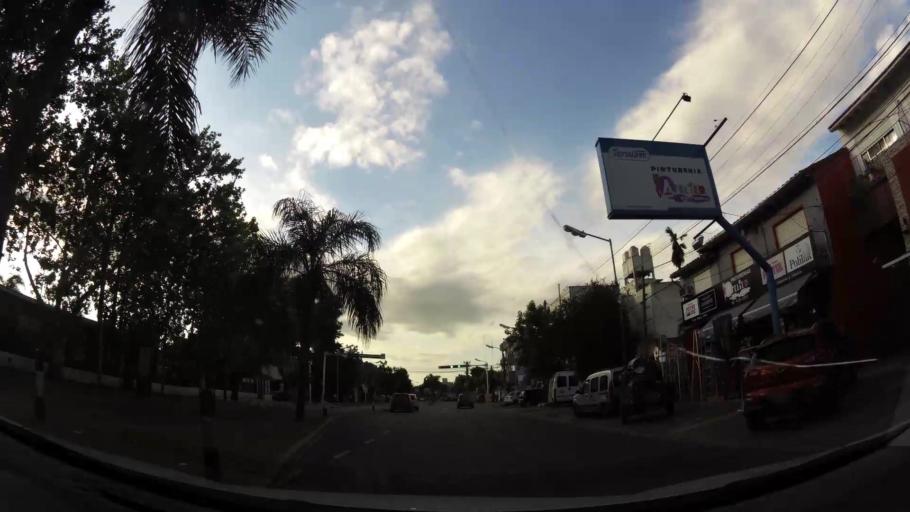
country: AR
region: Buenos Aires
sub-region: Partido de Tigre
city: Tigre
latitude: -34.4607
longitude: -58.6296
